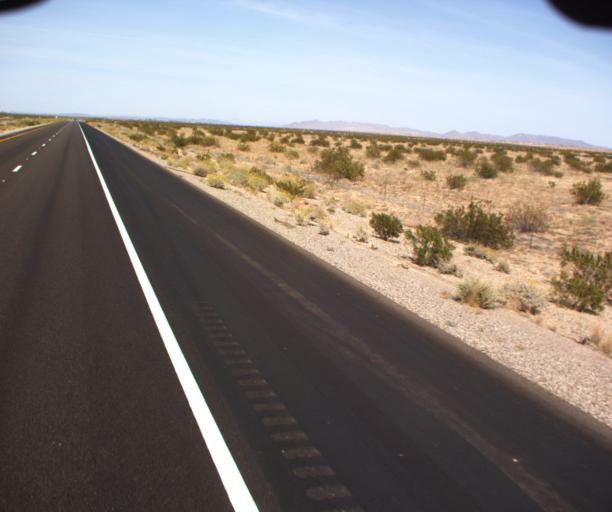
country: US
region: Arizona
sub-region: Yuma County
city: Fortuna Foothills
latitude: 32.5825
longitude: -114.5515
